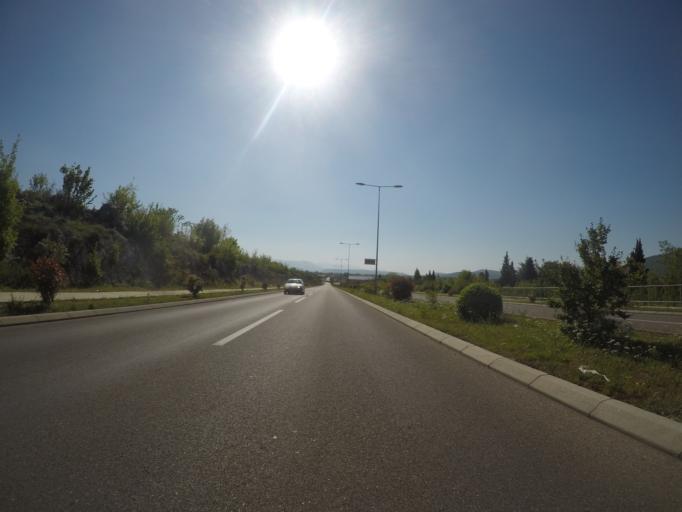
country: ME
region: Danilovgrad
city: Danilovgrad
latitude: 42.5492
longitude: 19.0952
